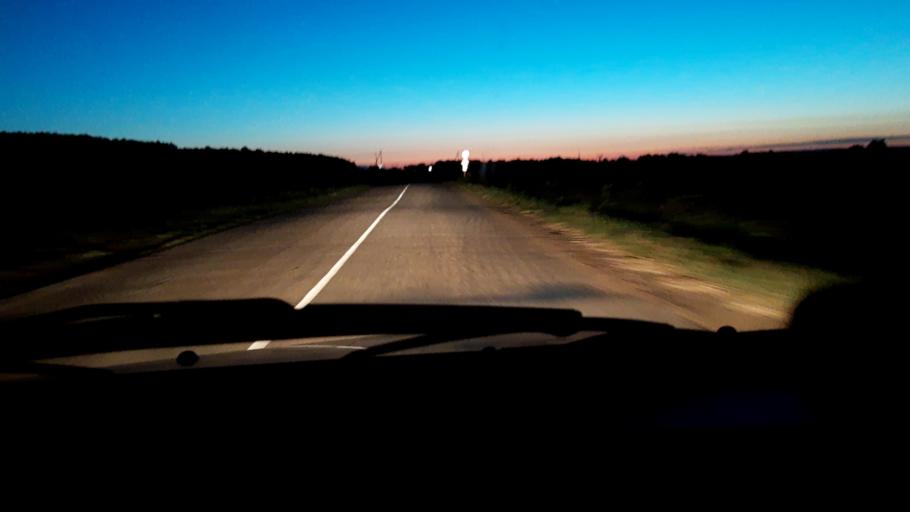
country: RU
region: Bashkortostan
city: Blagoveshchensk
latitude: 54.9335
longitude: 55.9002
